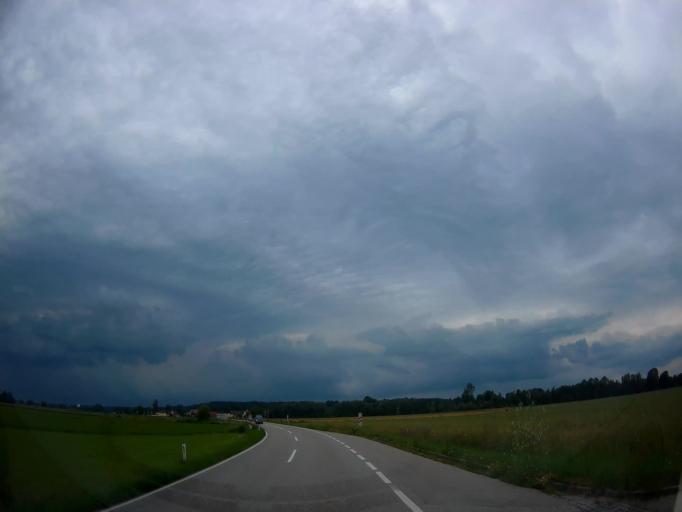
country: AT
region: Upper Austria
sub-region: Politischer Bezirk Braunau am Inn
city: Braunau am Inn
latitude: 48.1829
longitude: 13.1312
